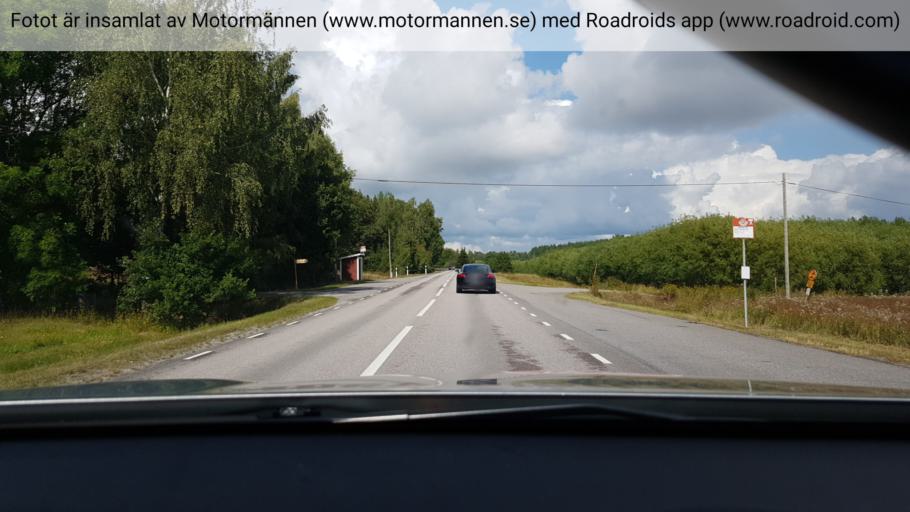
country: SE
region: Stockholm
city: Stenhamra
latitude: 59.3527
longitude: 17.6241
